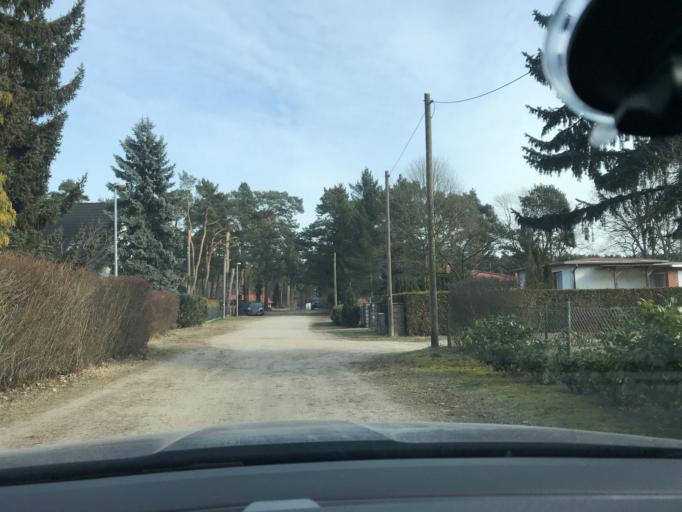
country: DE
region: Brandenburg
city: Erkner
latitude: 52.3898
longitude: 13.7708
